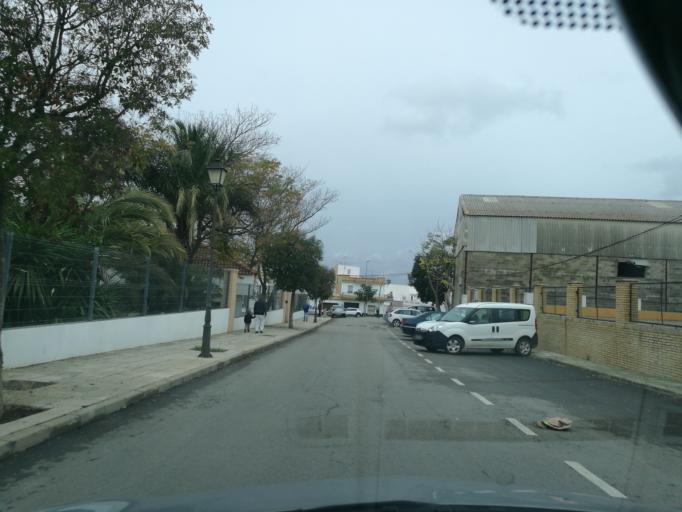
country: ES
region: Andalusia
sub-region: Provincia de Sevilla
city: La Campana
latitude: 37.5652
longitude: -5.4274
